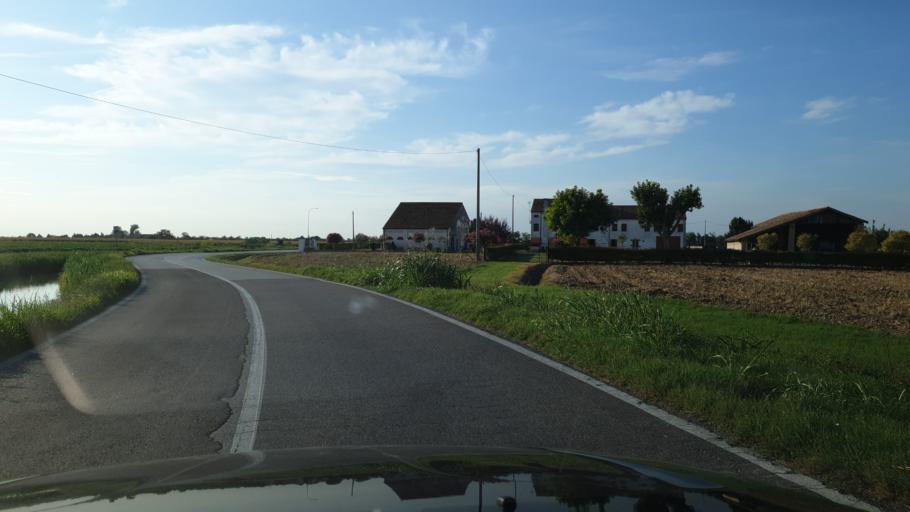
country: IT
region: Veneto
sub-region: Provincia di Rovigo
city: Fiesso Umbertiano
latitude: 44.9799
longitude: 11.6089
